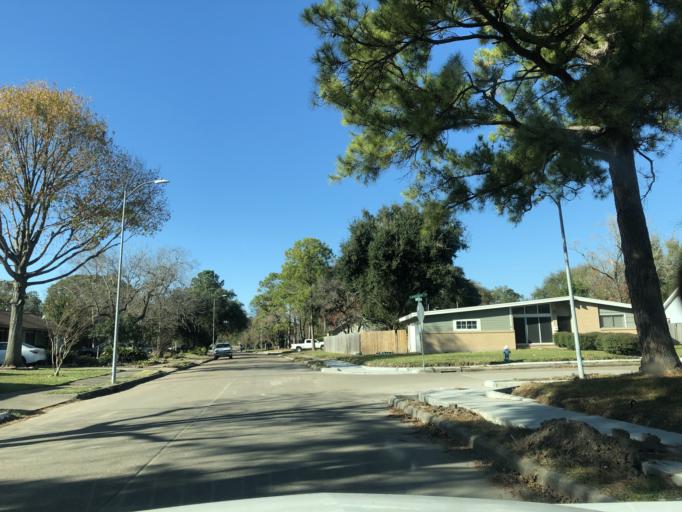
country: US
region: Texas
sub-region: Harris County
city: Bellaire
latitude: 29.6943
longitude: -95.5099
